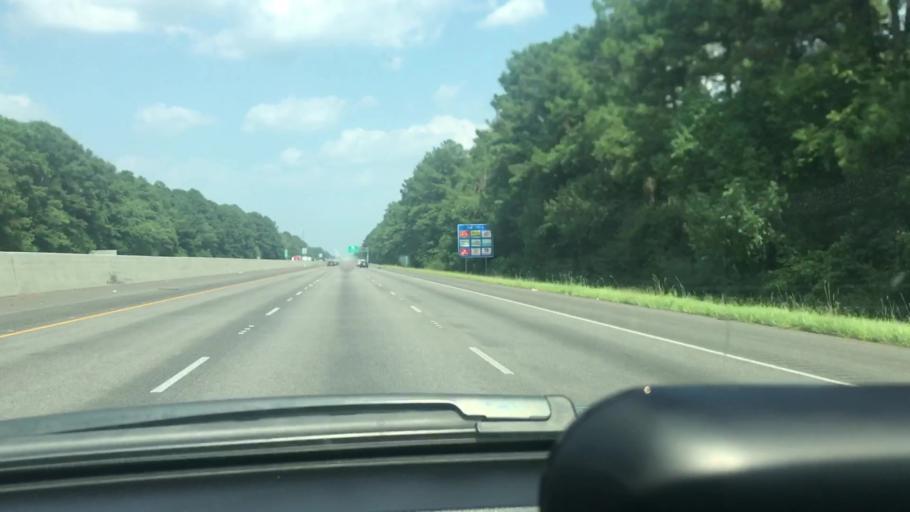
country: US
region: Louisiana
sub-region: Livingston Parish
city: Walker
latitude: 30.4678
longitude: -90.8799
